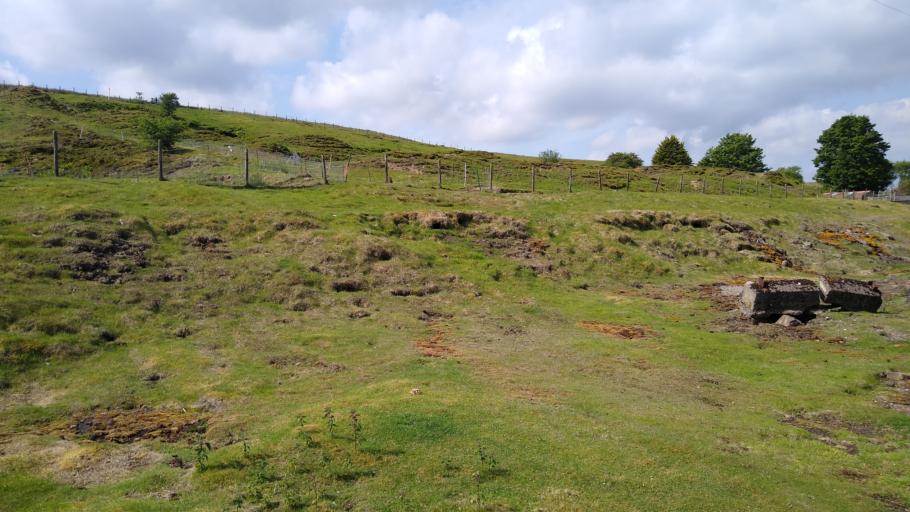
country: GB
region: England
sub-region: Northumberland
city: Greenhead
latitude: 54.9251
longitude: -2.5974
